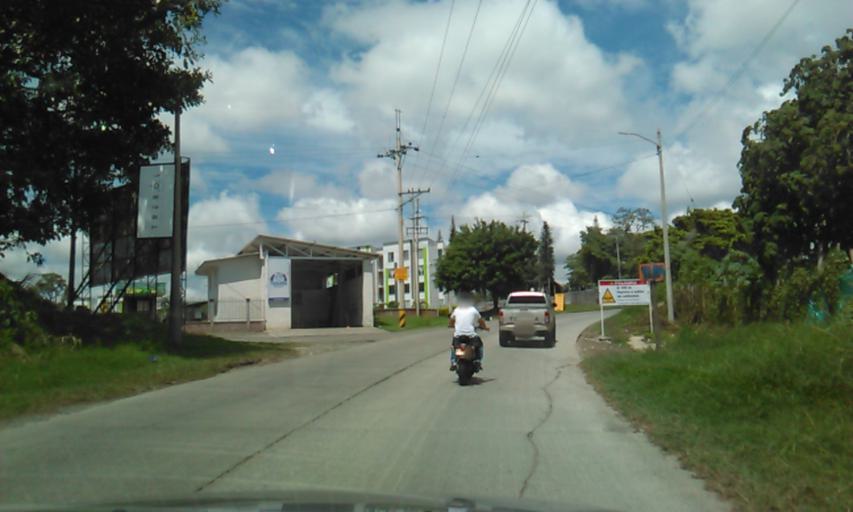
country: CO
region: Quindio
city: Armenia
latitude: 4.5053
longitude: -75.6910
